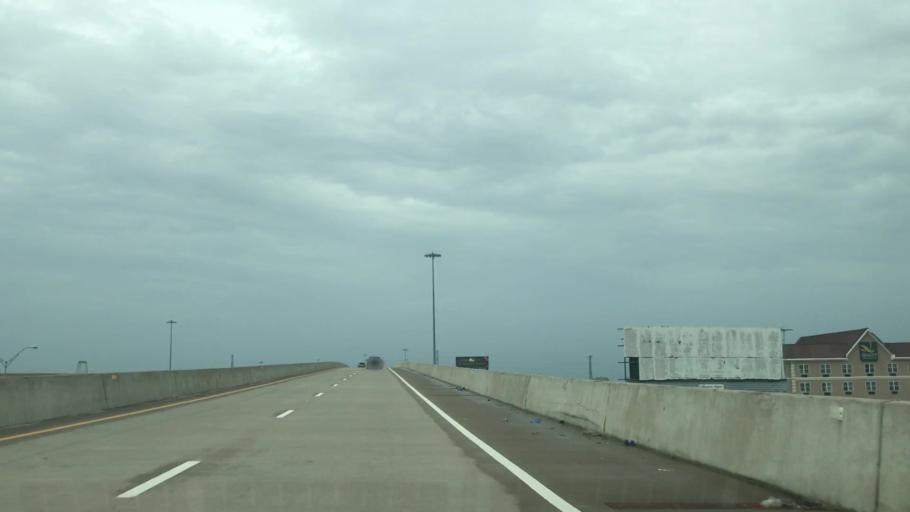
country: US
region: Texas
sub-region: Dallas County
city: Farmers Branch
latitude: 32.8762
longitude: -96.8975
